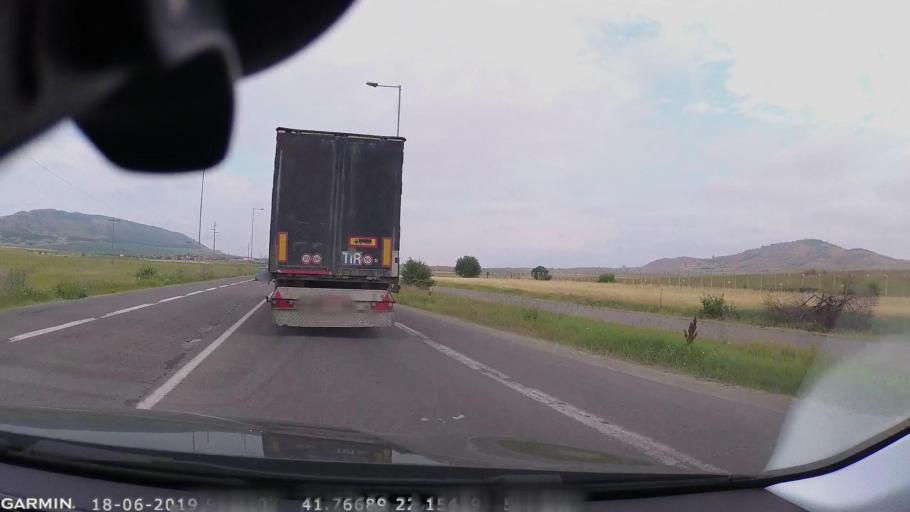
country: MK
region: Stip
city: Shtip
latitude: 41.7671
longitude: 22.1541
